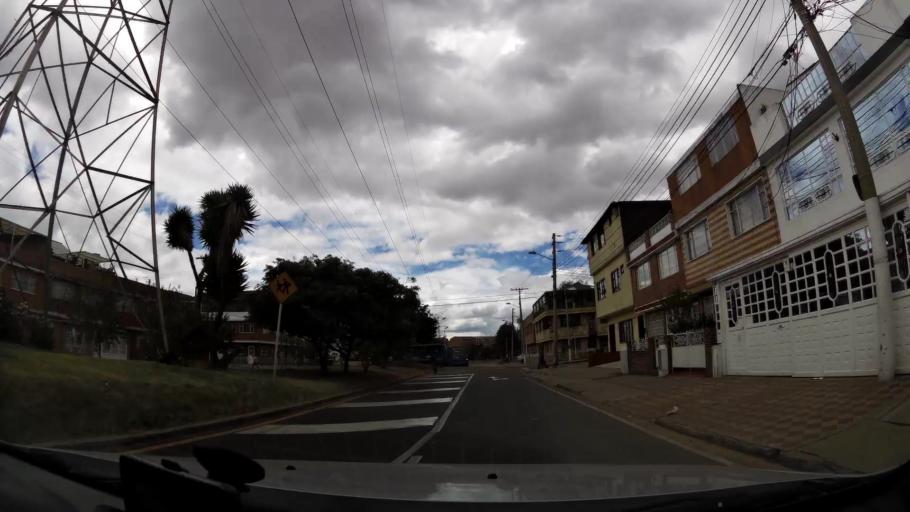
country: CO
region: Bogota D.C.
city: Bogota
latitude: 4.6135
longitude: -74.1218
